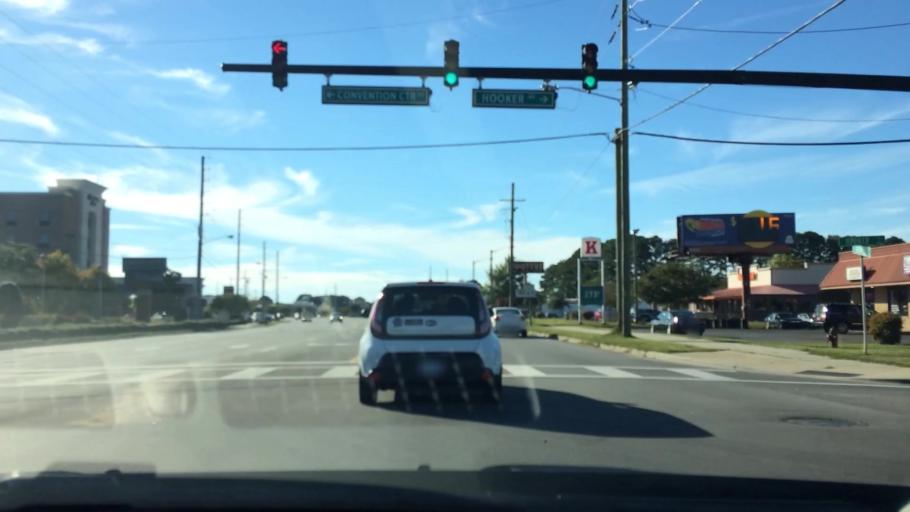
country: US
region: North Carolina
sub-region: Pitt County
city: Summerfield
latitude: 35.5744
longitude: -77.3904
